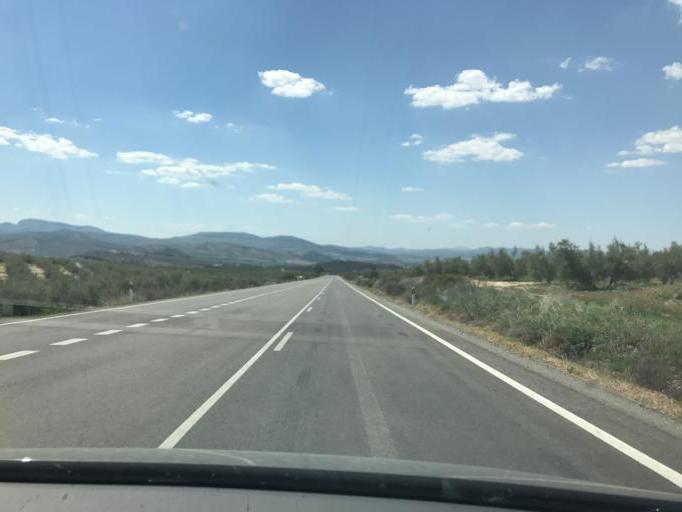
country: ES
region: Andalusia
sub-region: Provincia de Jaen
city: Frailes
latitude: 37.4314
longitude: -3.7816
